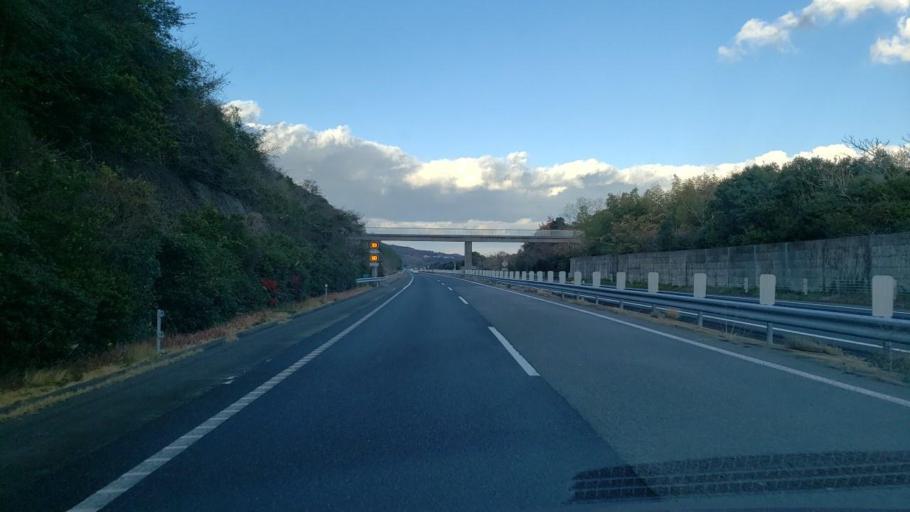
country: JP
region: Hyogo
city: Sumoto
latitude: 34.3305
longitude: 134.8294
